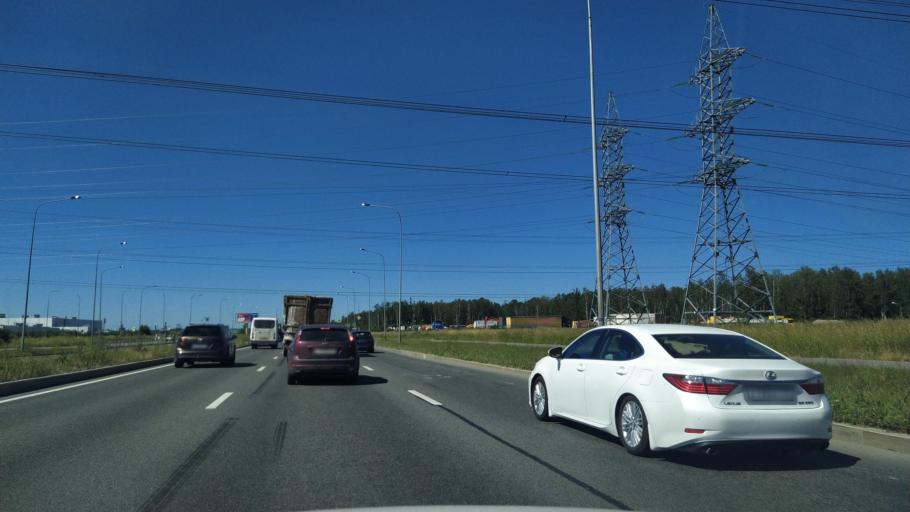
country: RU
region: St.-Petersburg
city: Levashovo
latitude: 60.0633
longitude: 30.1945
